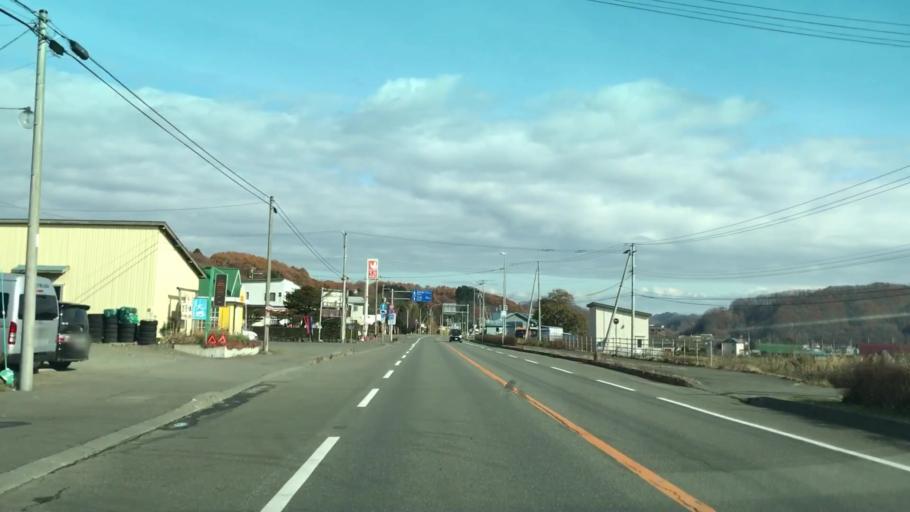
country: JP
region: Hokkaido
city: Shizunai-furukawacho
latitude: 42.5812
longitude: 142.1226
